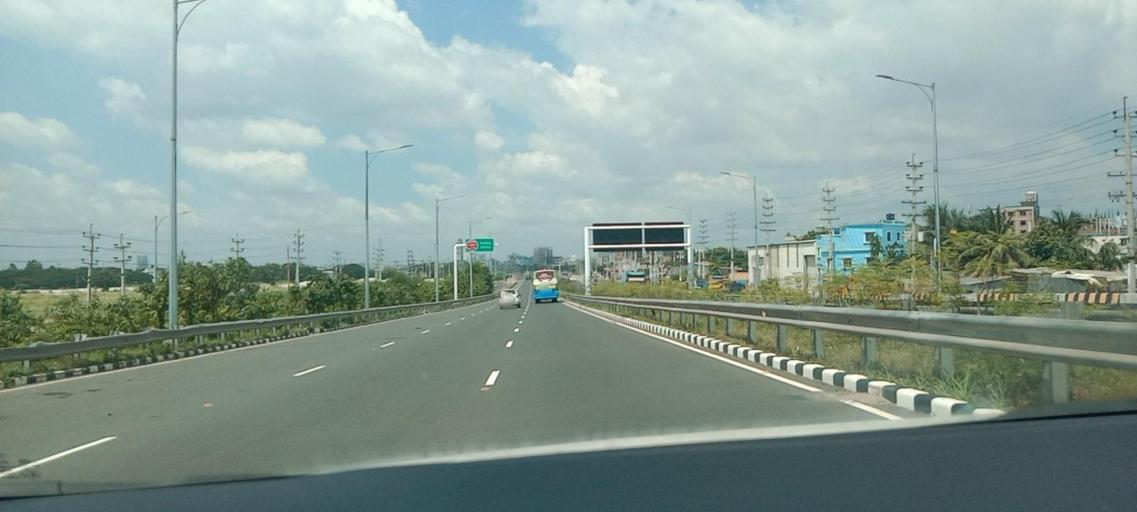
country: BD
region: Dhaka
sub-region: Dhaka
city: Dhaka
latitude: 23.6765
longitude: 90.4068
